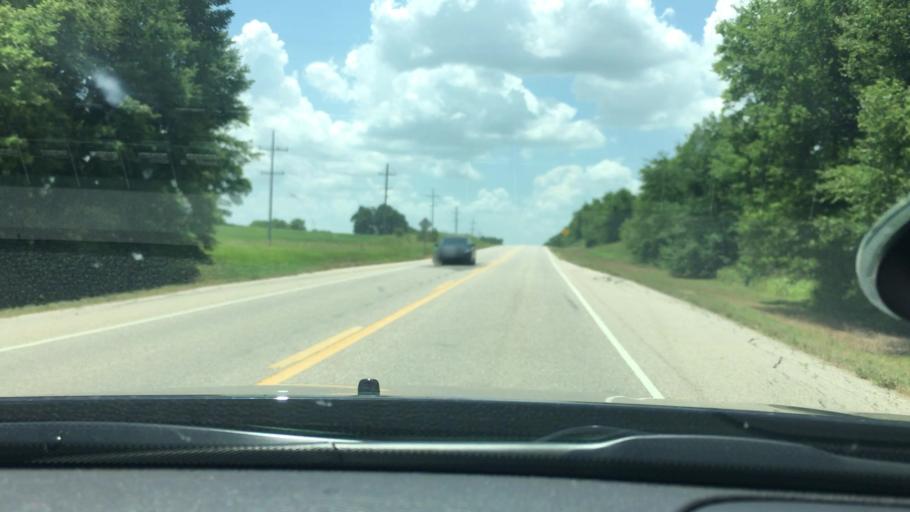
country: US
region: Oklahoma
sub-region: Pontotoc County
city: Ada
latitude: 34.6834
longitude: -96.6349
